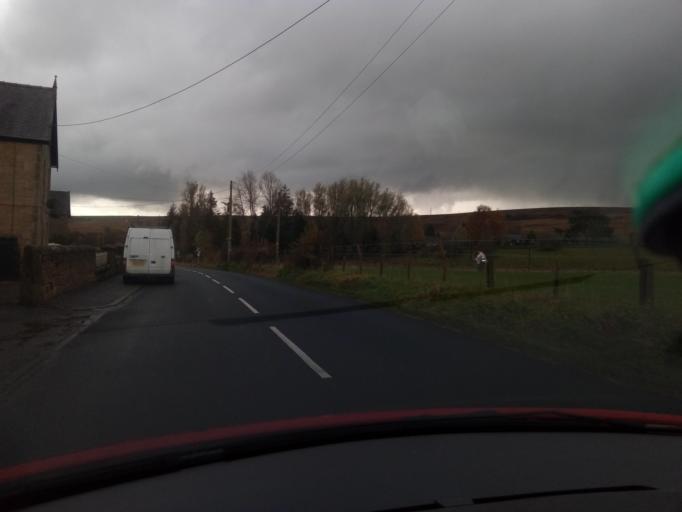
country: GB
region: England
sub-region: Northumberland
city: Birtley
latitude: 55.1403
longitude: -2.2616
